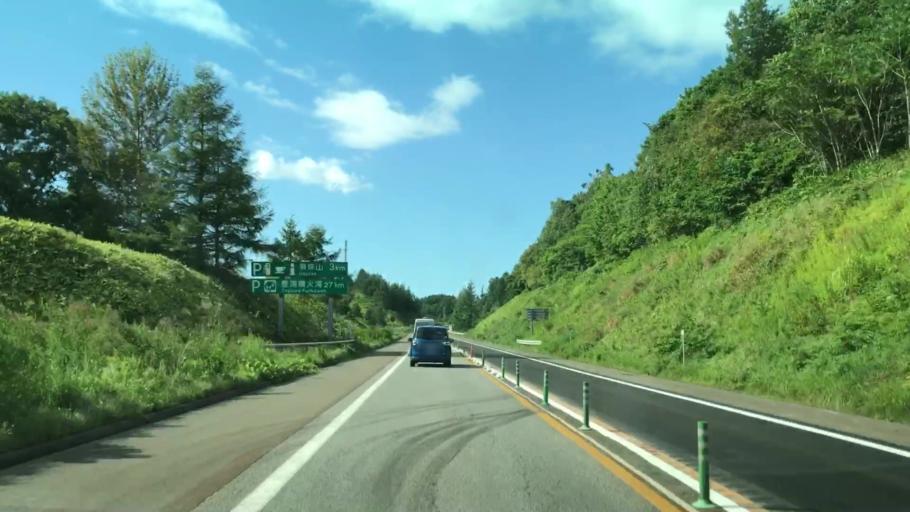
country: JP
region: Hokkaido
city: Date
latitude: 42.4392
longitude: 140.9190
